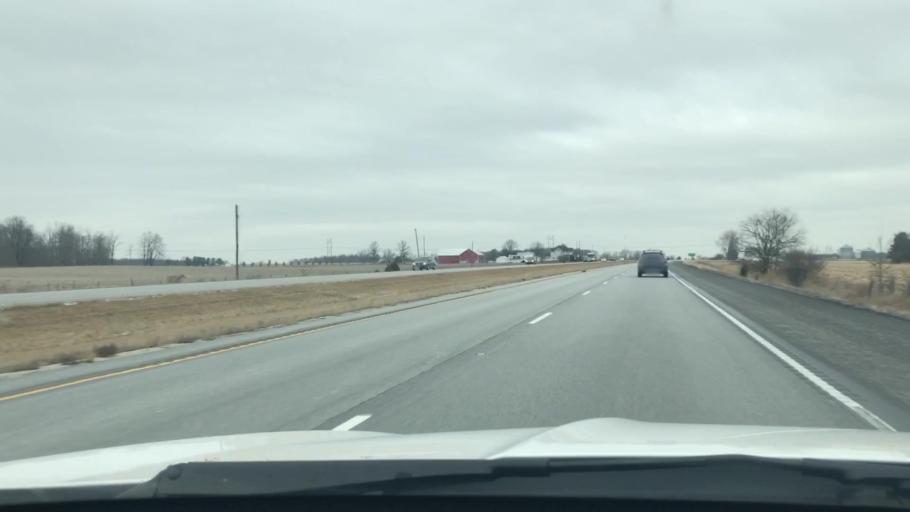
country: US
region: Indiana
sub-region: Miami County
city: Peru
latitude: 40.8610
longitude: -86.1345
